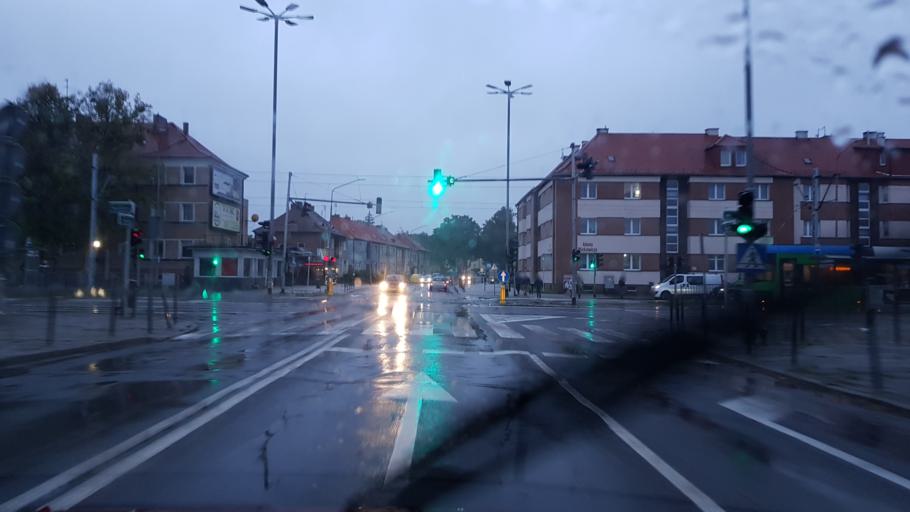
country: PL
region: West Pomeranian Voivodeship
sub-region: Szczecin
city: Szczecin
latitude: 53.4411
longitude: 14.5137
